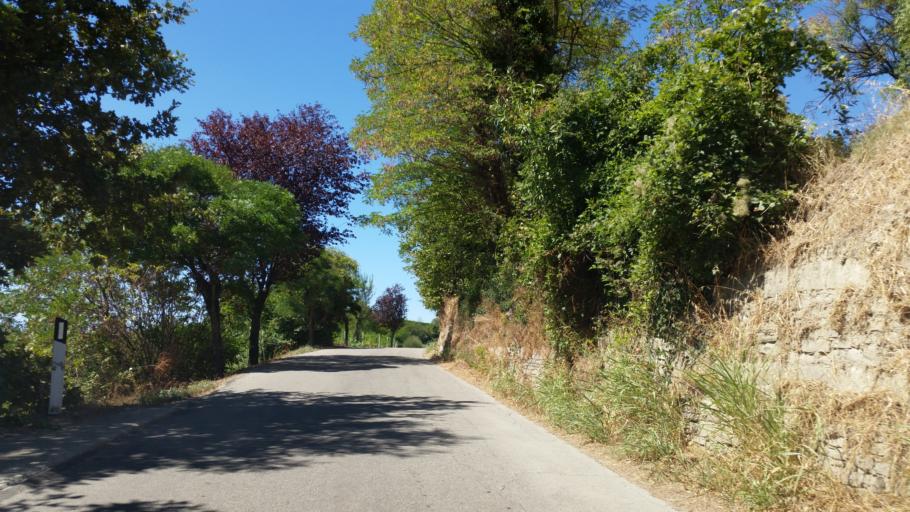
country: IT
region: Piedmont
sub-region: Provincia di Cuneo
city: Neive-Borgonovo
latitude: 44.7256
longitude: 8.1123
